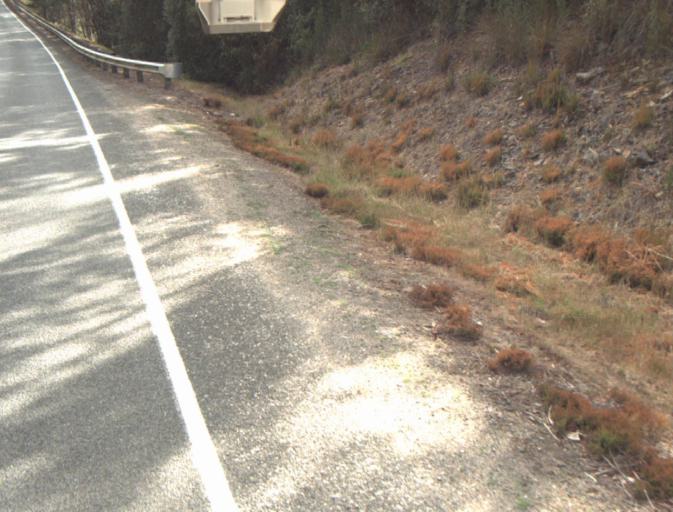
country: AU
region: Tasmania
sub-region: Launceston
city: Mayfield
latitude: -41.2965
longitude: 147.2128
